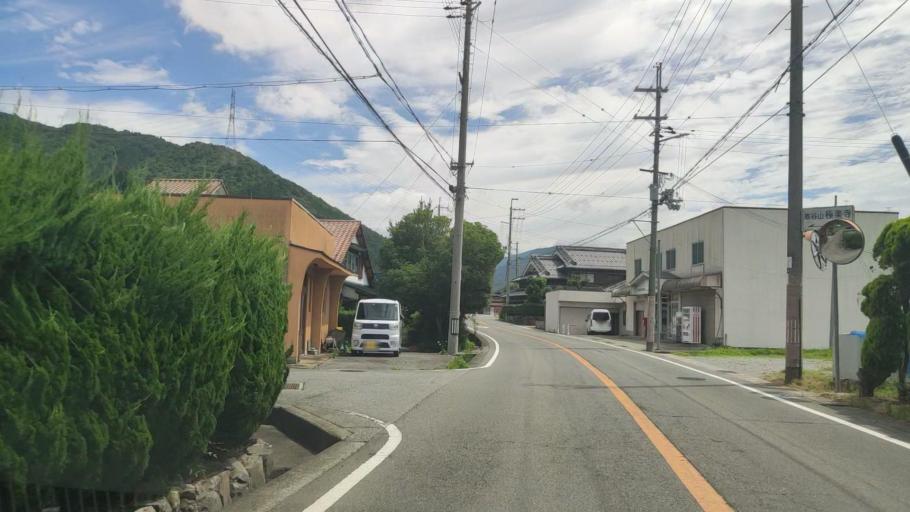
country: JP
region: Hyogo
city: Nishiwaki
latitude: 35.1083
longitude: 134.9059
